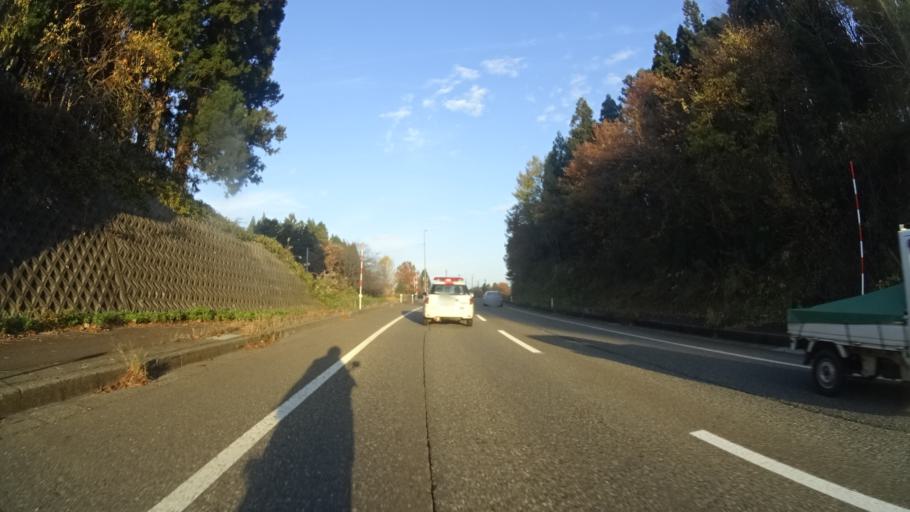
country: JP
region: Niigata
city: Nagaoka
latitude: 37.4495
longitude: 138.7474
